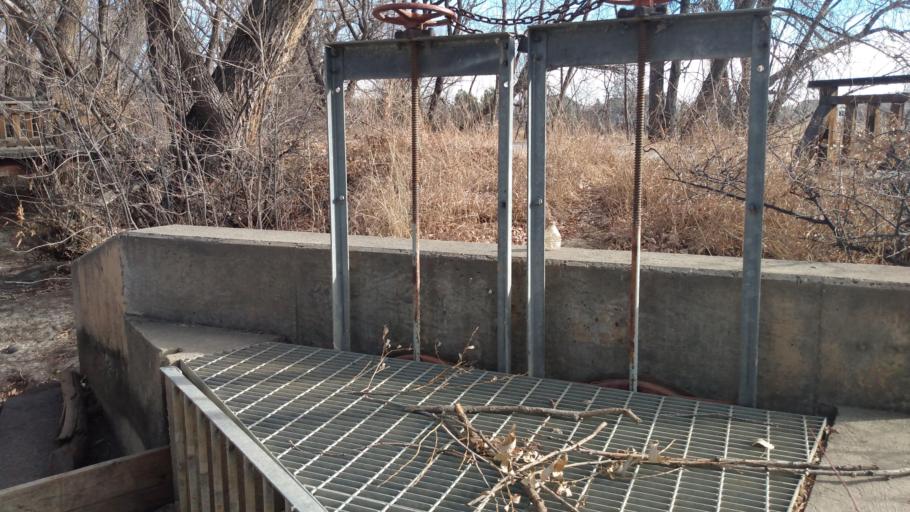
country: US
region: Colorado
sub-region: Boulder County
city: Gunbarrel
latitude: 40.0608
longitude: -105.1987
